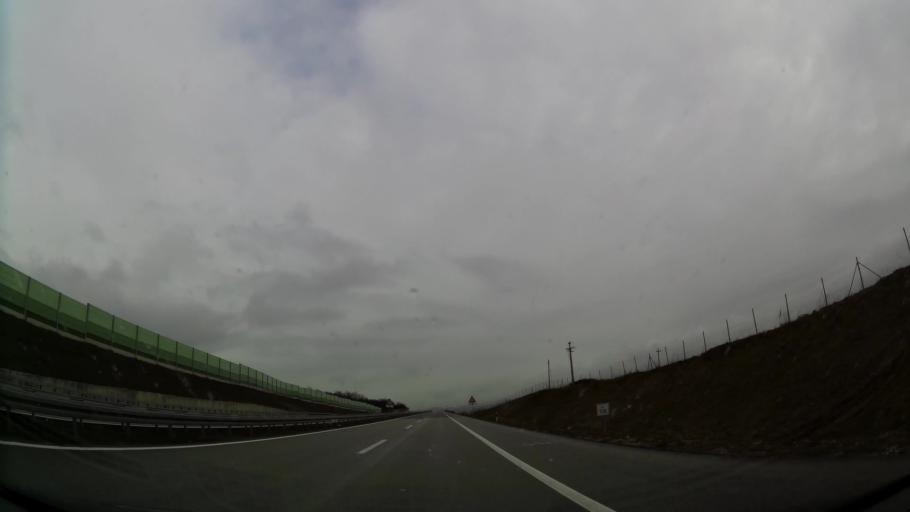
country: RS
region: Central Serbia
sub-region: Pcinjski Okrug
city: Vranjska Banja
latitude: 42.5655
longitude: 21.9614
